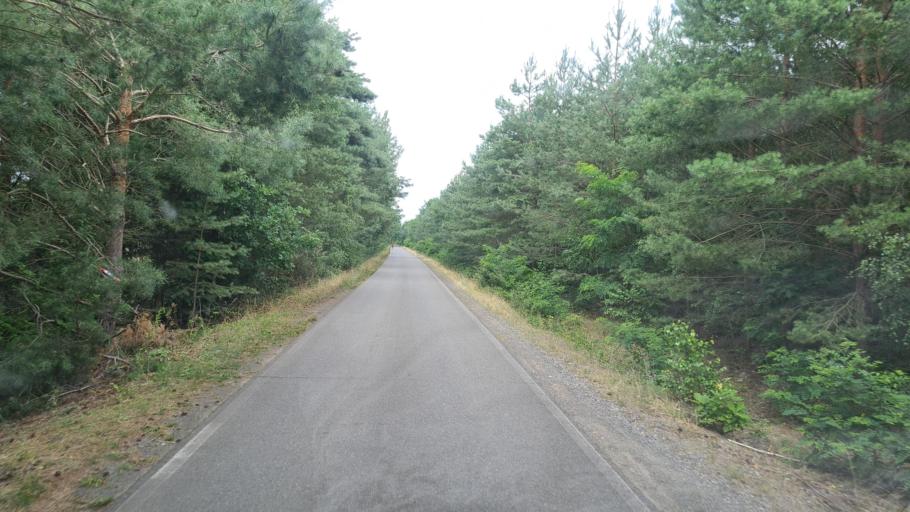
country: DE
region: Brandenburg
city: Neupetershain
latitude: 51.6725
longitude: 14.1141
